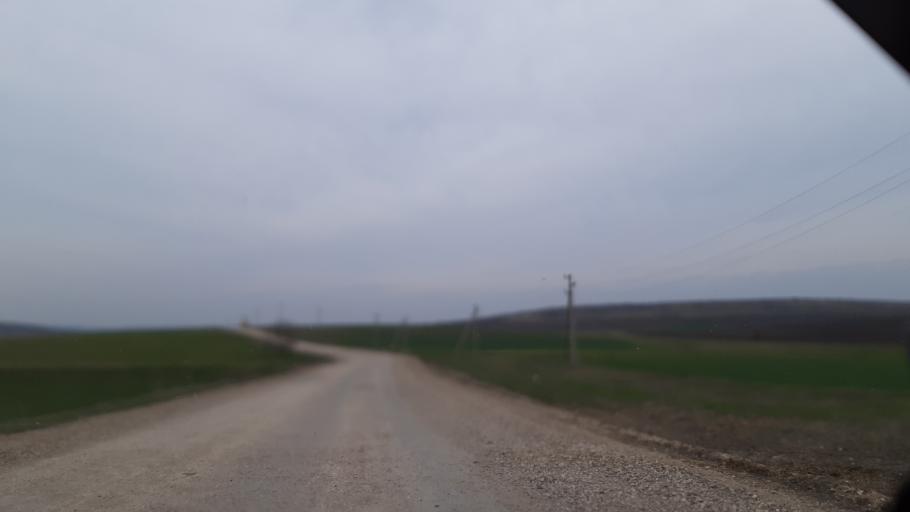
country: MD
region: Soldanesti
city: Soldanesti
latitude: 47.6200
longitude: 28.6579
